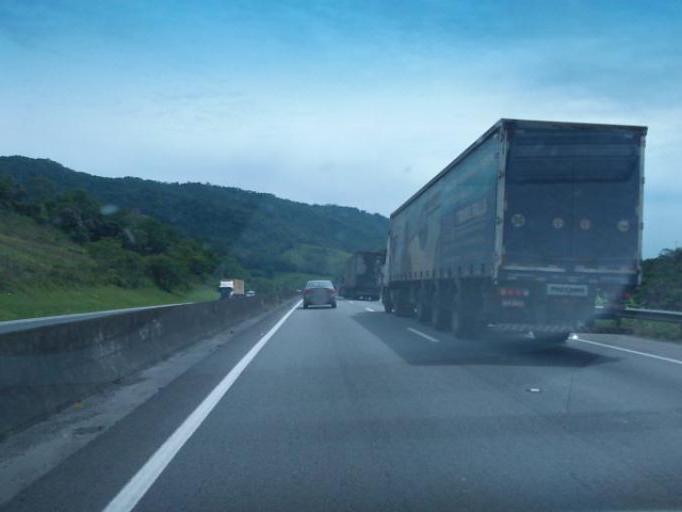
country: BR
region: Sao Paulo
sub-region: Miracatu
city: Miracatu
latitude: -24.2990
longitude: -47.4833
